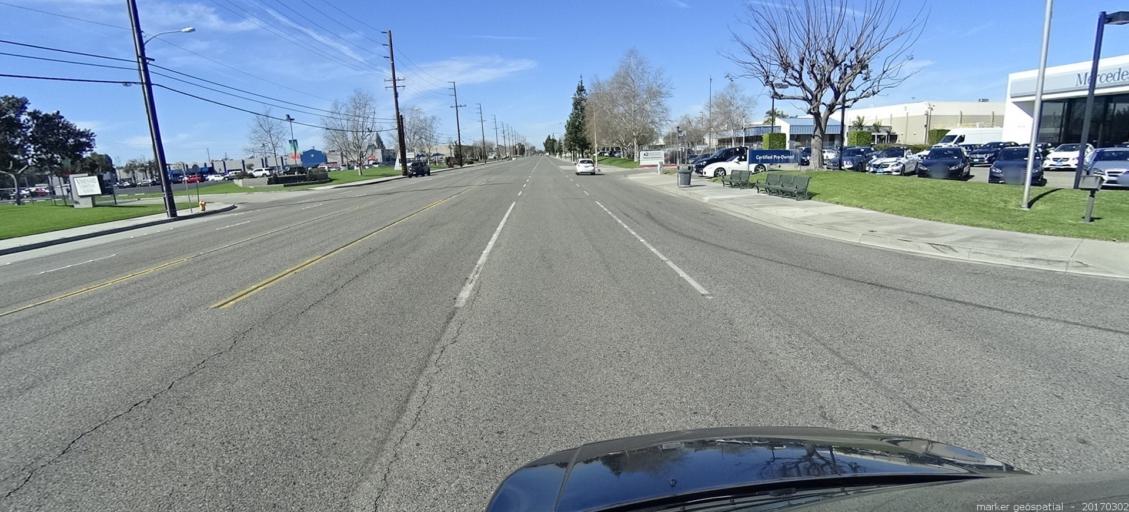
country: US
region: California
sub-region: Orange County
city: Yorba Linda
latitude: 33.8596
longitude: -117.7990
